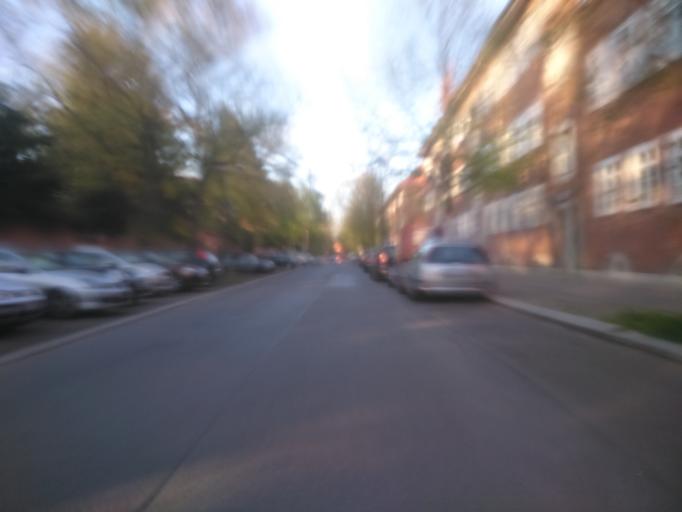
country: DE
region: Berlin
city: Weissensee
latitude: 52.5553
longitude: 13.4538
